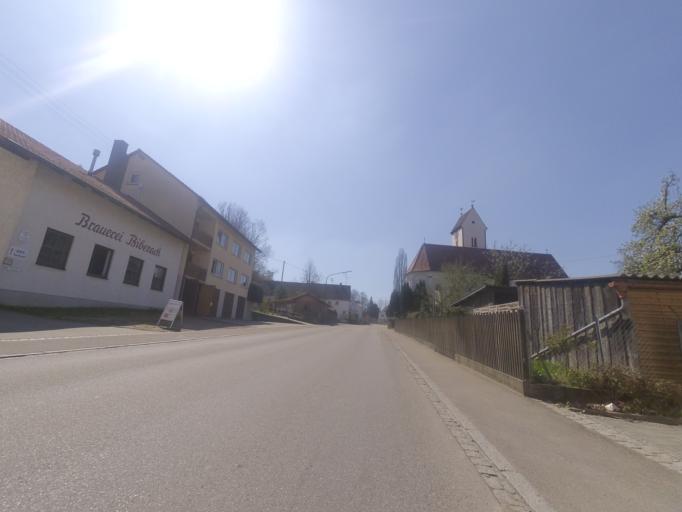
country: DE
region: Bavaria
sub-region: Swabia
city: Roggenburg
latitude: 48.2877
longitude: 10.2202
